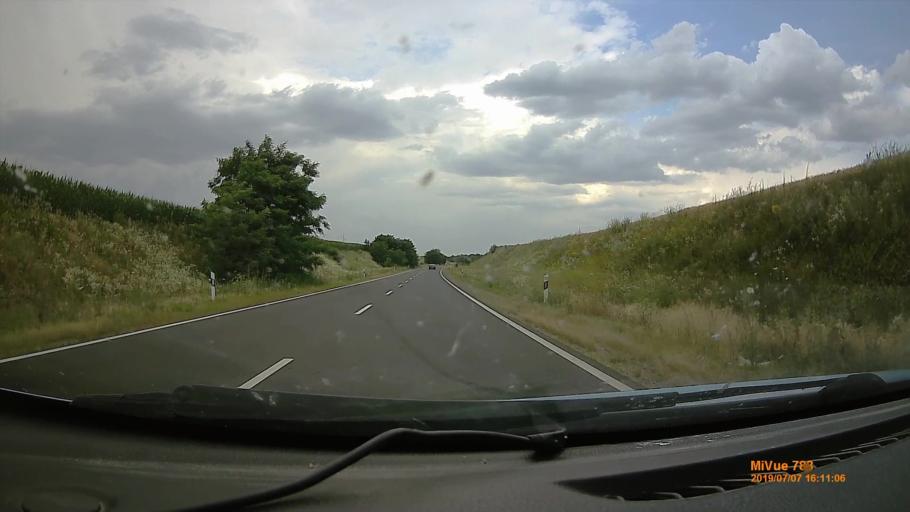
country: HU
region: Heves
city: Hatvan
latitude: 47.6725
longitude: 19.7174
